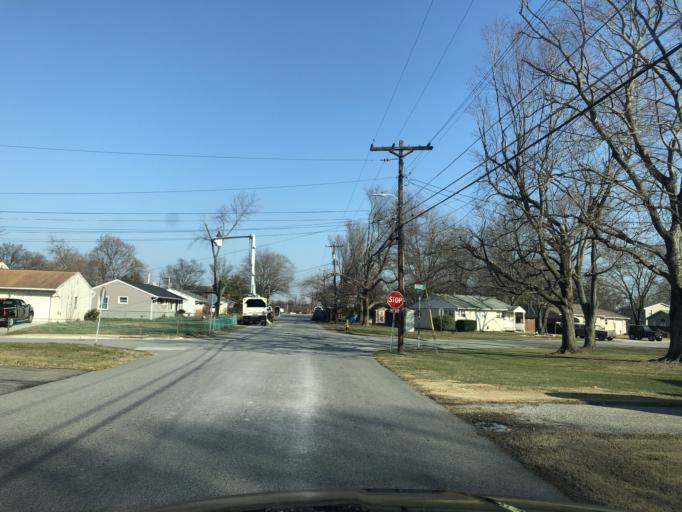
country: US
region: Maryland
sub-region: Anne Arundel County
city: Odenton
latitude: 39.0779
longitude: -76.6950
